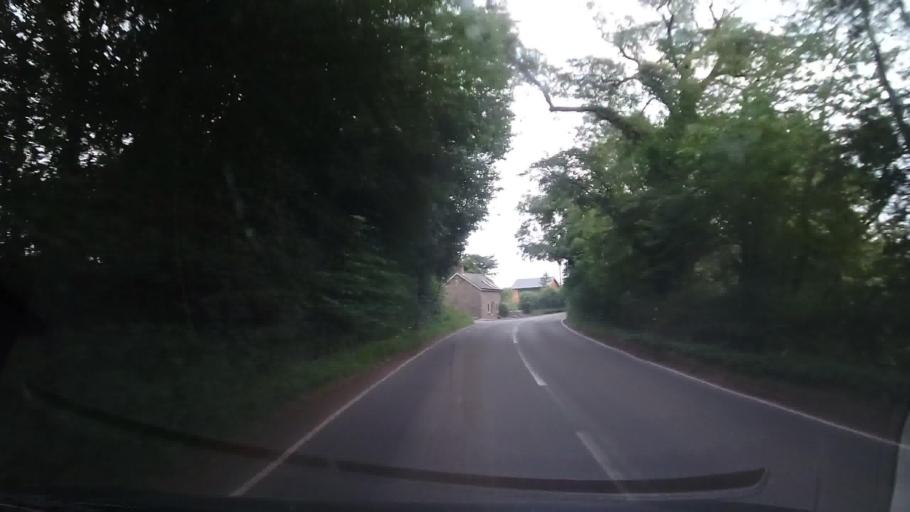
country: GB
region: Wales
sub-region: Sir Powys
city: Llanfechain
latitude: 52.8071
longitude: -3.1399
